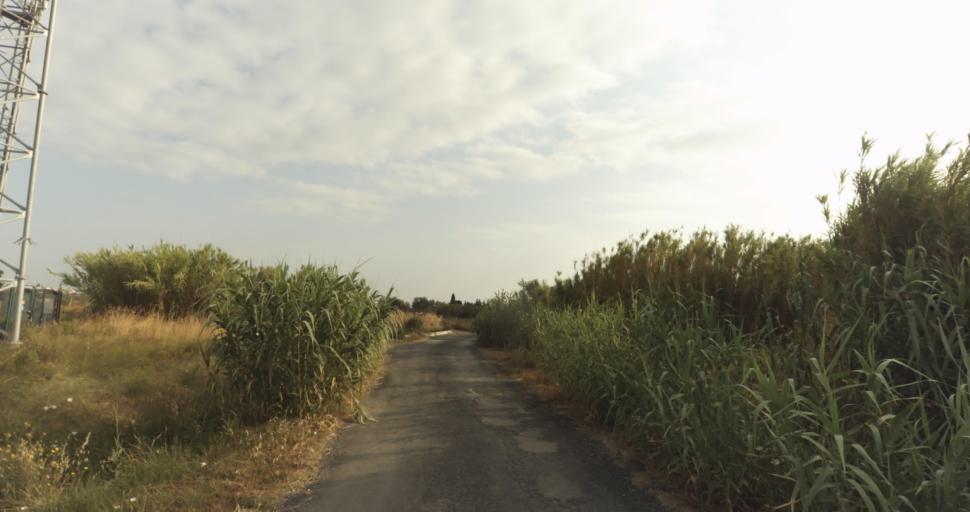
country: FR
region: Languedoc-Roussillon
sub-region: Departement des Pyrenees-Orientales
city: Villeneuve-de-la-Raho
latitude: 42.6254
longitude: 2.9308
